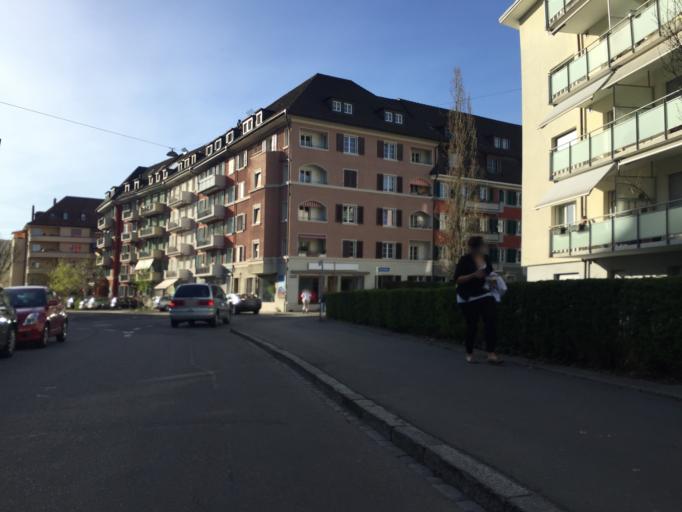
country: CH
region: Bern
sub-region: Bern-Mittelland District
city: Bern
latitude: 46.9547
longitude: 7.4329
